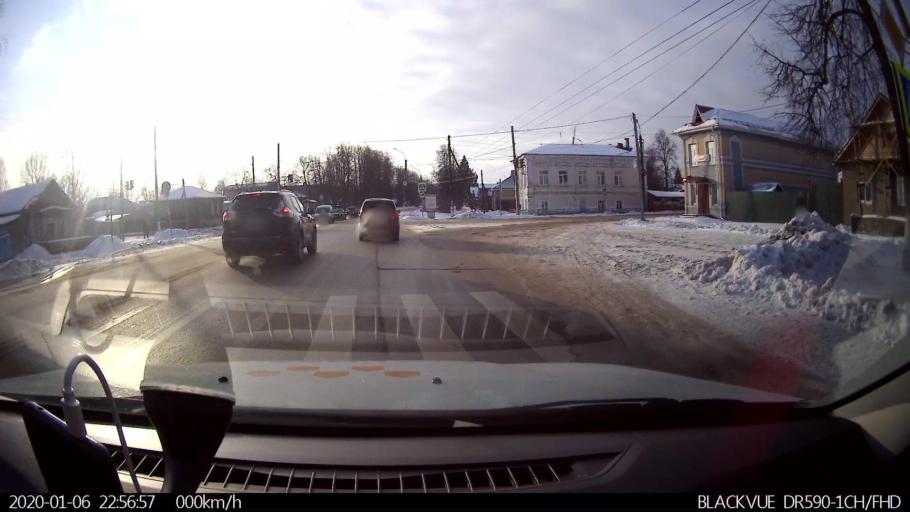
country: RU
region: Nizjnij Novgorod
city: Bogorodsk
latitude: 56.1096
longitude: 43.5289
